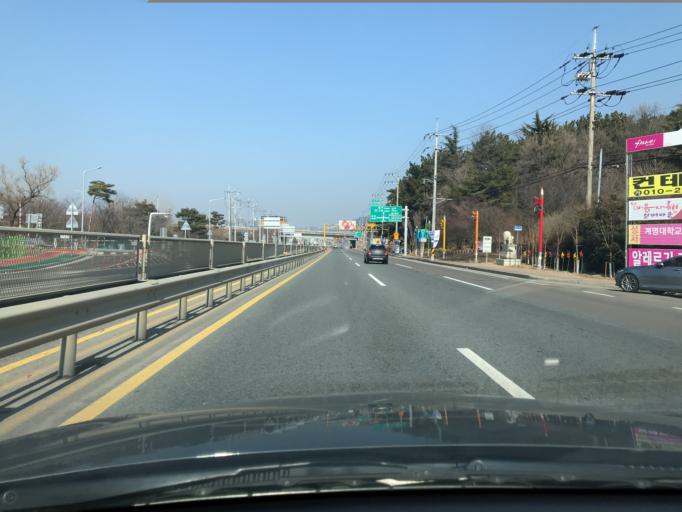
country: KR
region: Daegu
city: Hwawon
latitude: 35.7025
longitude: 128.4391
